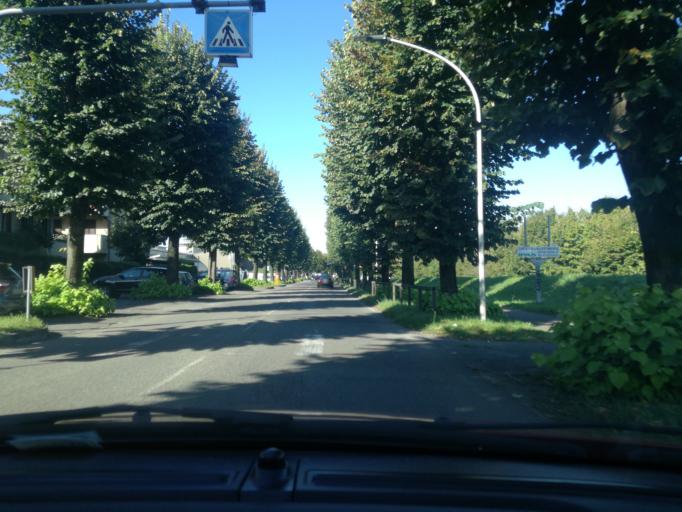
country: IT
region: Lombardy
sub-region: Provincia di Monza e Brianza
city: Seregno
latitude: 45.6561
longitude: 9.1870
